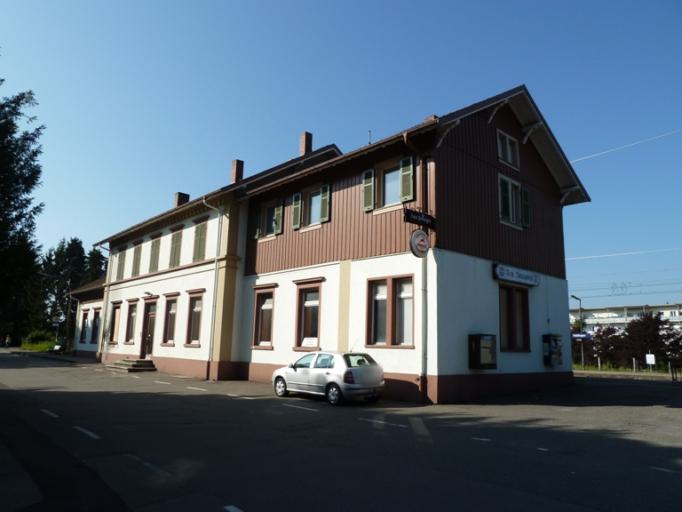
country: DE
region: Baden-Wuerttemberg
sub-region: Freiburg Region
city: Binzen
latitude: 47.6132
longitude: 7.6119
